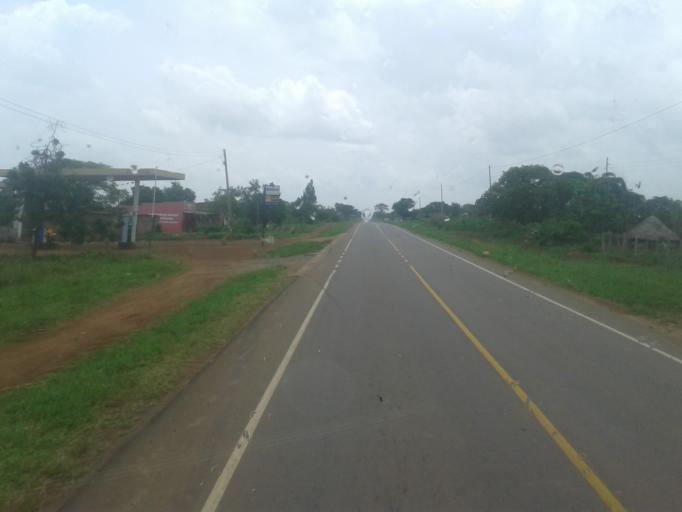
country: UG
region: Western Region
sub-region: Kiryandongo District
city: Masindi Port
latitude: 1.7066
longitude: 32.0290
